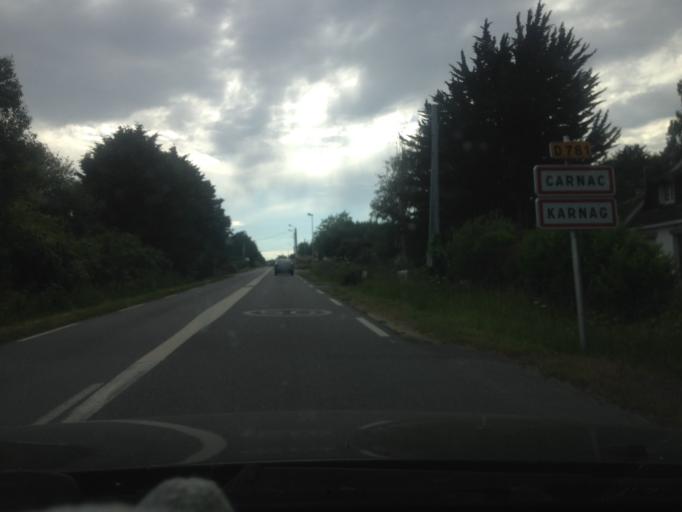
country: FR
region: Brittany
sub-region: Departement du Morbihan
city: Carnac
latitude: 47.5861
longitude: -3.0690
